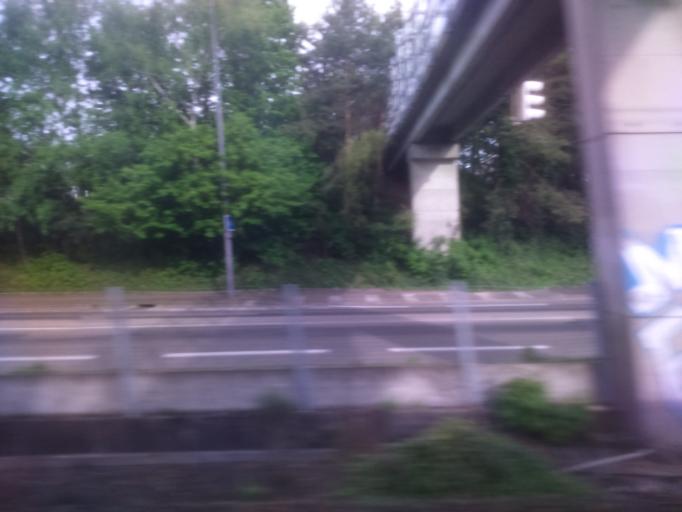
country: FR
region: Rhone-Alpes
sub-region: Departement de l'Isere
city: Grenoble
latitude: 45.1754
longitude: 5.7172
